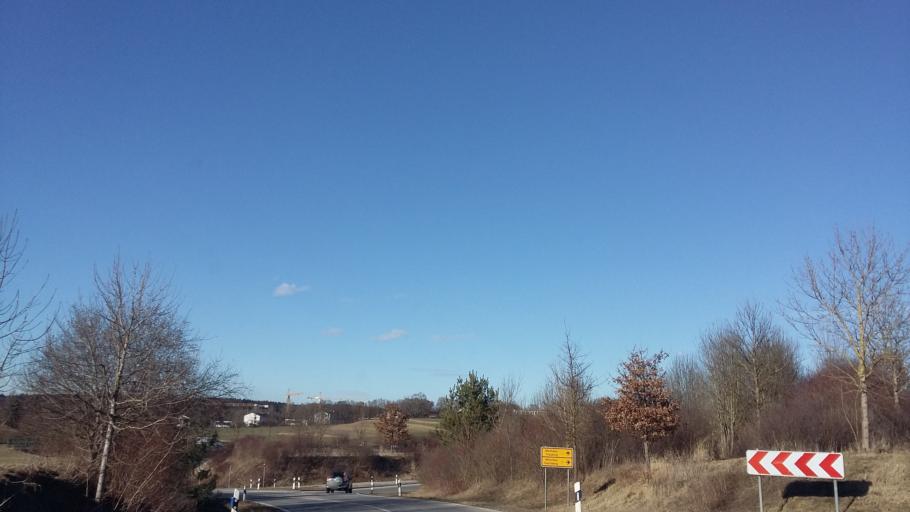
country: DE
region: Bavaria
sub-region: Upper Bavaria
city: Pocking
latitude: 47.9753
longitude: 11.3047
